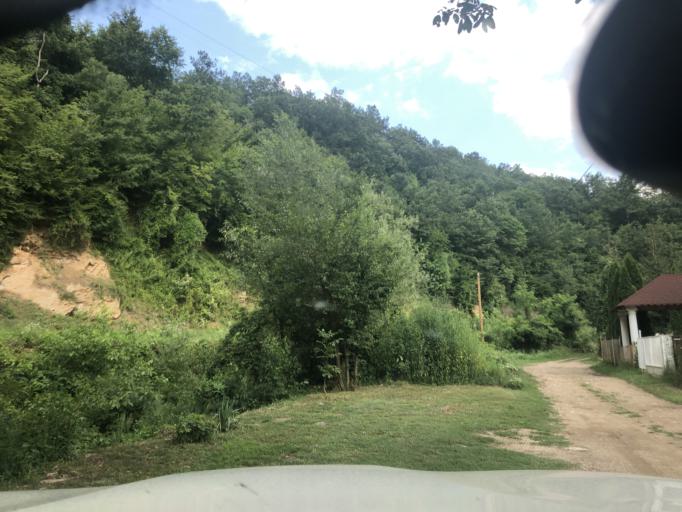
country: RS
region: Central Serbia
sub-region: Jablanicki Okrug
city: Medvega
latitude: 42.7876
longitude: 21.5863
